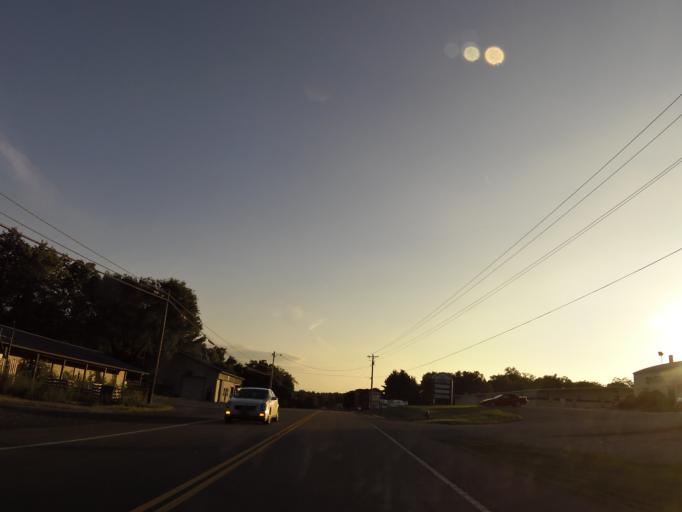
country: US
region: Tennessee
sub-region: Jefferson County
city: Dandridge
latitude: 36.0310
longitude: -83.3915
